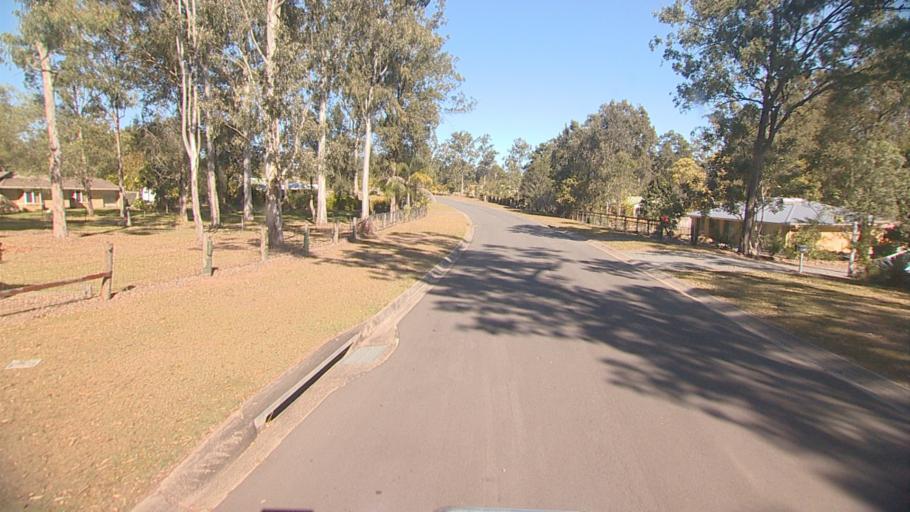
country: AU
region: Queensland
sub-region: Logan
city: North Maclean
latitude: -27.8221
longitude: 152.9437
